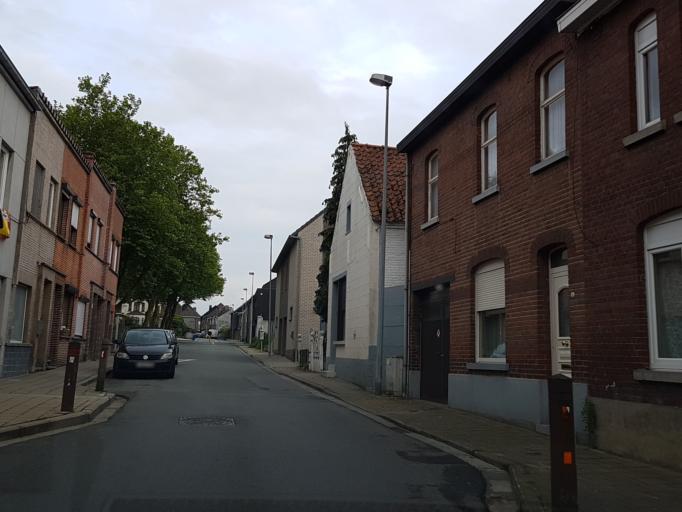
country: BE
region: Flanders
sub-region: Provincie Oost-Vlaanderen
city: Aalst
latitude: 50.9195
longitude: 4.0640
